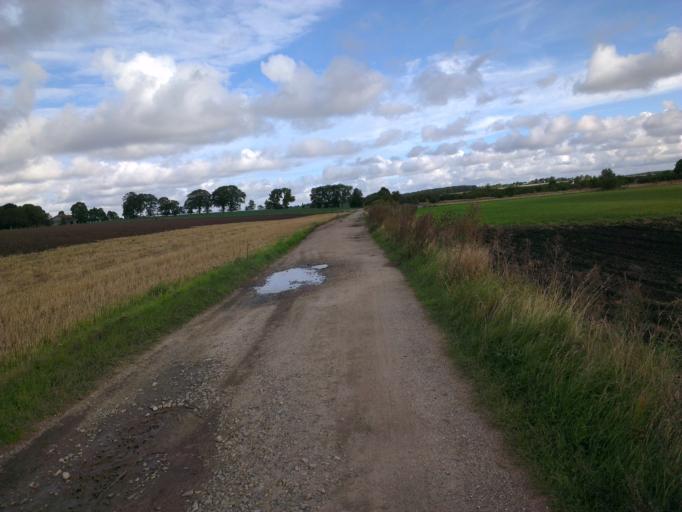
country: DK
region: Capital Region
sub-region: Frederikssund Kommune
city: Frederikssund
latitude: 55.8037
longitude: 12.0854
